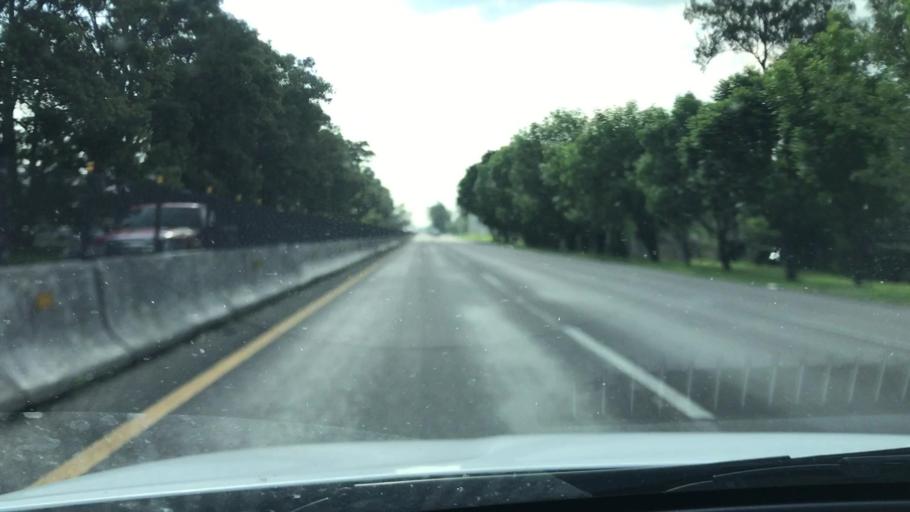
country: MX
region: Guanajuato
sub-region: Salamanca
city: El Divisador
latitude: 20.5535
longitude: -101.1519
